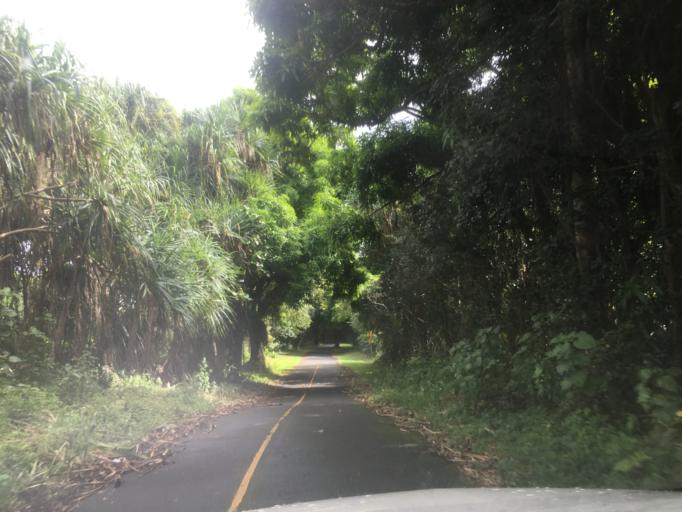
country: US
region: Hawaii
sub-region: Hawaii County
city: Leilani Estates
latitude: 19.4670
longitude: -154.8608
